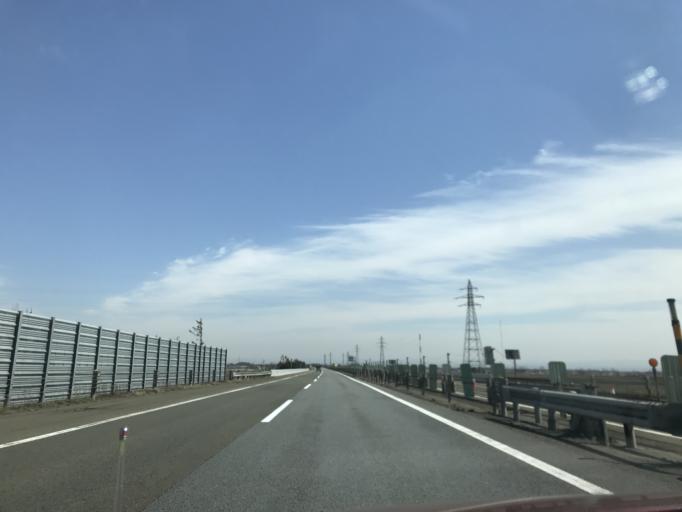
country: JP
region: Hokkaido
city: Ebetsu
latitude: 43.0840
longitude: 141.5576
